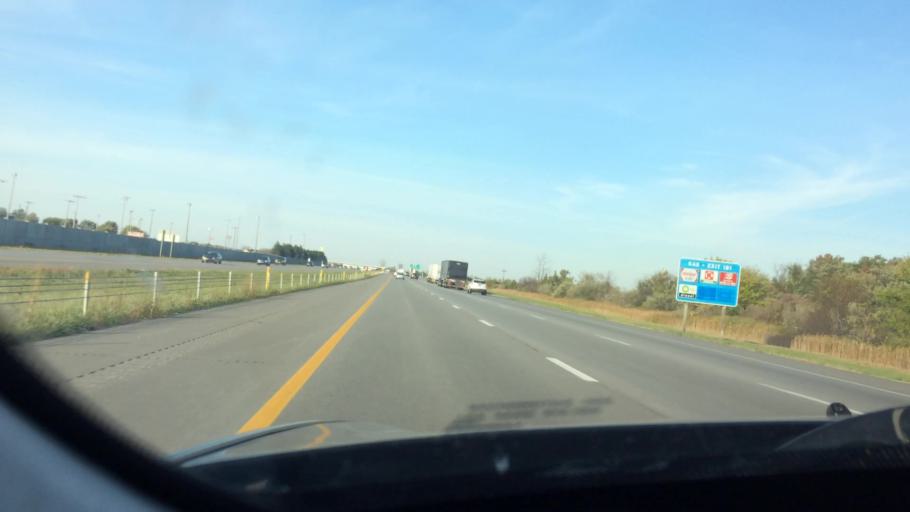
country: US
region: Ohio
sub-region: Wood County
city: Bowling Green
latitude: 41.3639
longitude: -83.6191
